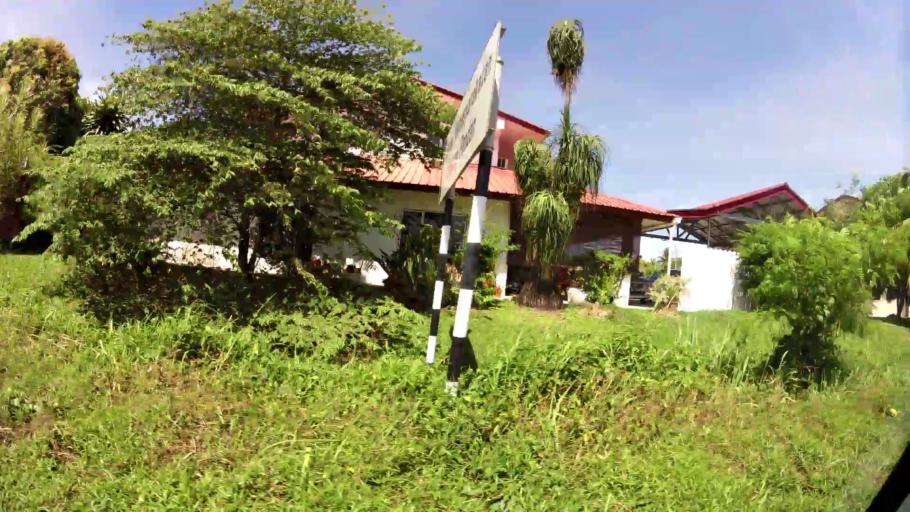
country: BN
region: Belait
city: Kuala Belait
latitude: 4.5846
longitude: 114.2192
